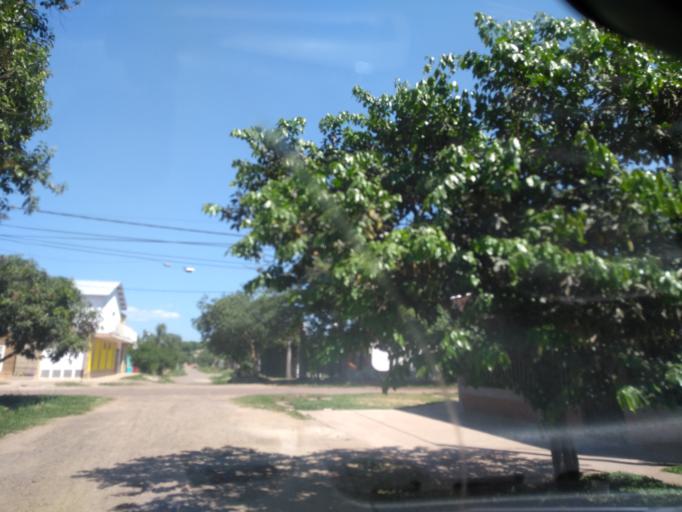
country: AR
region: Chaco
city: Fontana
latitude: -27.4114
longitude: -59.0351
